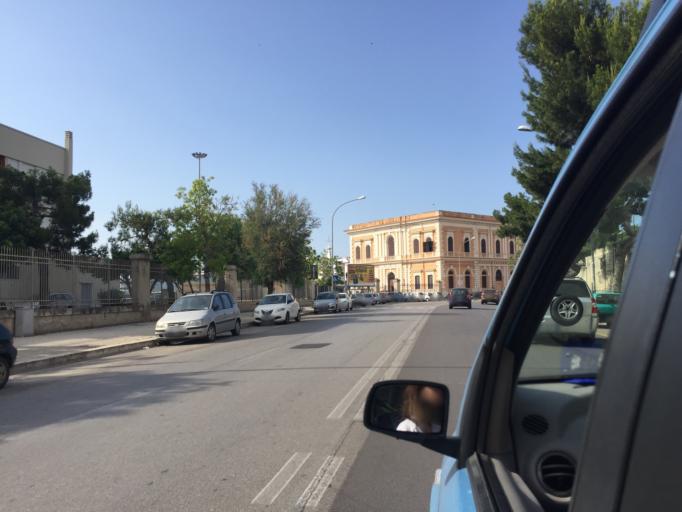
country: IT
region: Apulia
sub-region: Provincia di Bari
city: Bari
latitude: 41.1308
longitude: 16.8677
